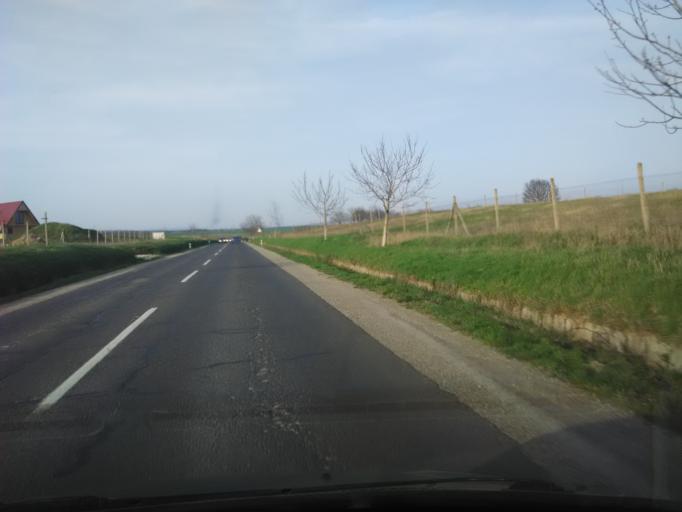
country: SK
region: Nitriansky
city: Surany
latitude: 48.0944
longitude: 18.2928
